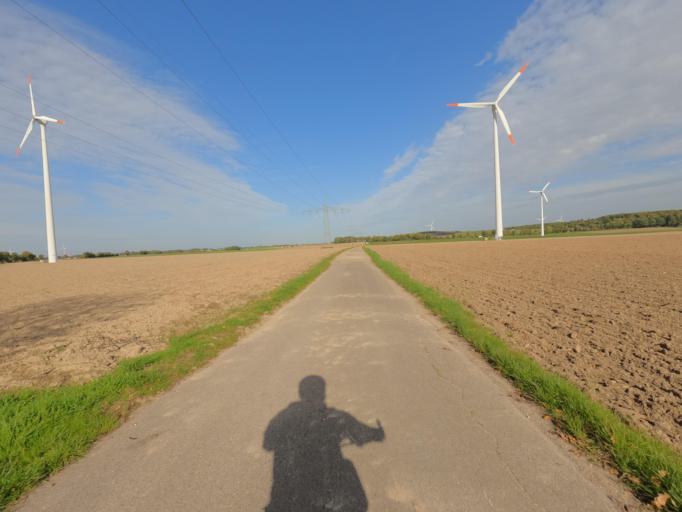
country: DE
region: North Rhine-Westphalia
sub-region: Regierungsbezirk Koln
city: Gangelt
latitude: 50.9896
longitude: 6.0588
